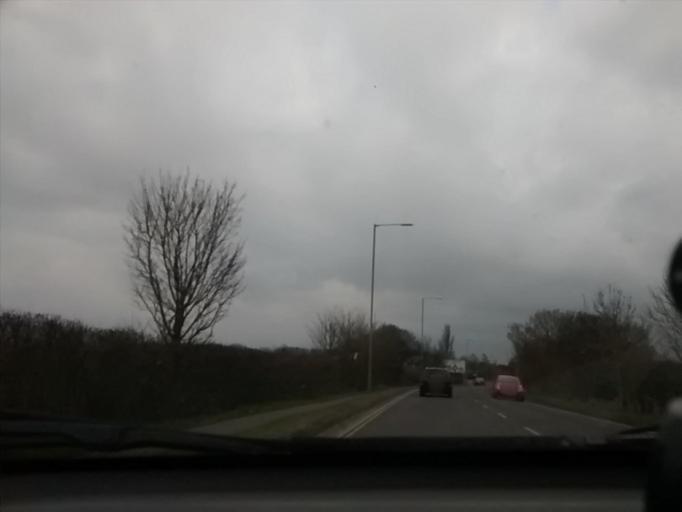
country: GB
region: England
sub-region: Cambridgeshire
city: Cambridge
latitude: 52.1695
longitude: 0.1545
